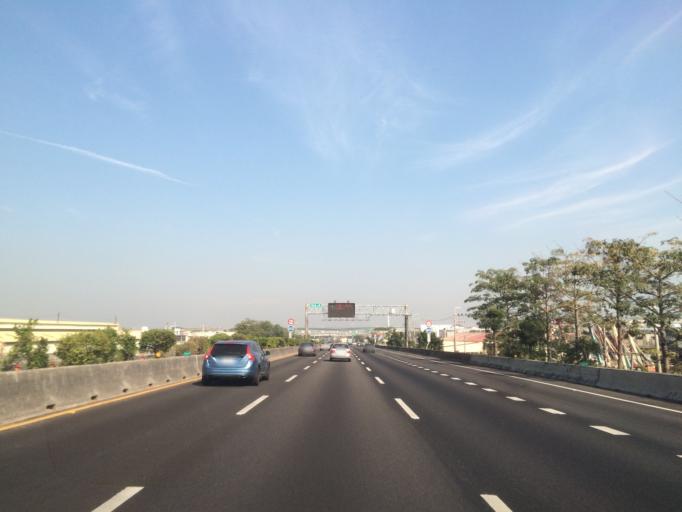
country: TW
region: Taiwan
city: Fengyuan
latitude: 24.2595
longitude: 120.6916
